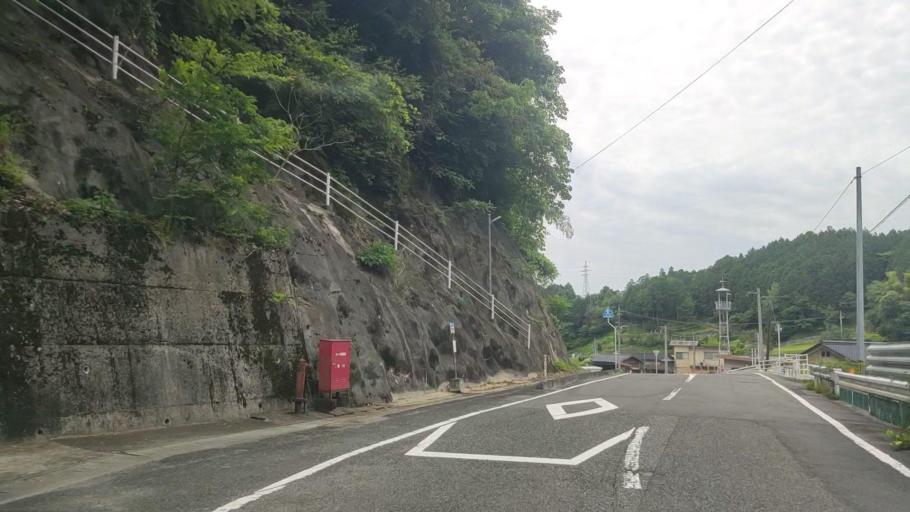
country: JP
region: Hyogo
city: Yamazakicho-nakabirose
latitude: 35.0926
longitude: 134.2821
